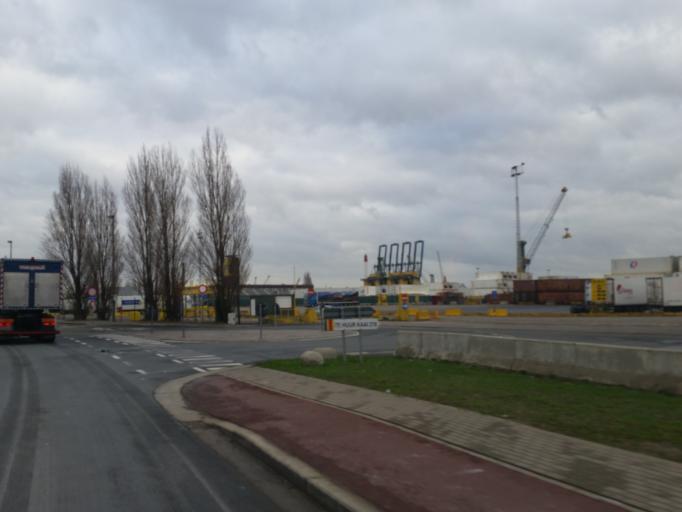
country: BE
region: Flanders
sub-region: Provincie Antwerpen
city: Antwerpen
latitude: 51.2648
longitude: 4.3766
